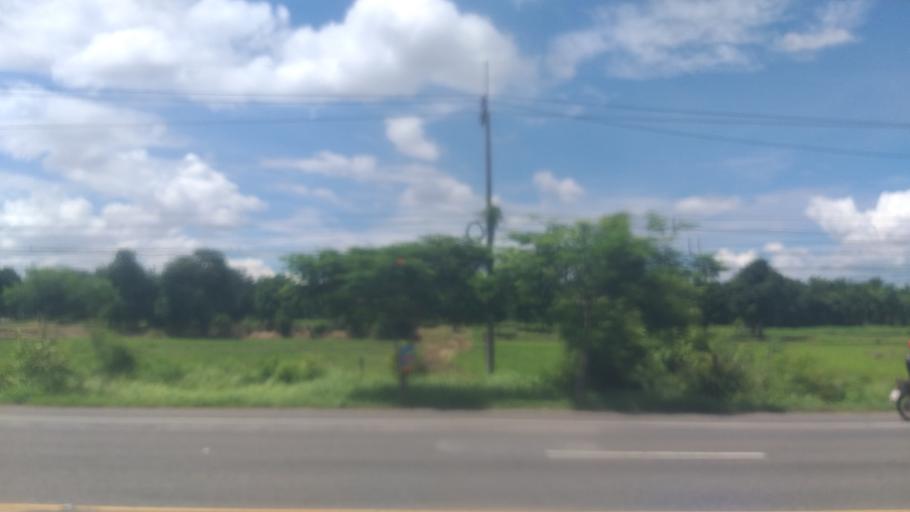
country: TH
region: Nakhon Ratchasima
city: Phra Thong Kham
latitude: 15.2996
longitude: 101.9810
